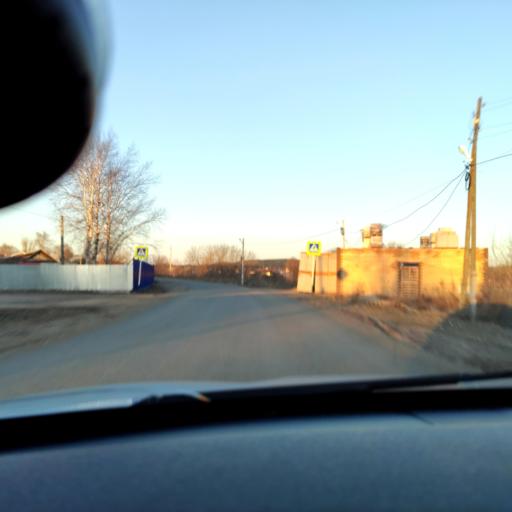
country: RU
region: Perm
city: Kultayevo
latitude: 57.9340
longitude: 55.8798
